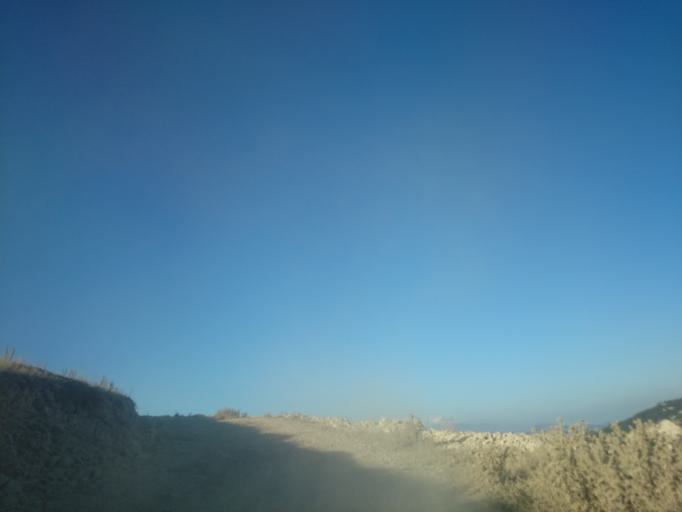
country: AL
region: Berat
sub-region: Rrethi i Skraparit
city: Bogove
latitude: 40.6101
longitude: 20.1895
